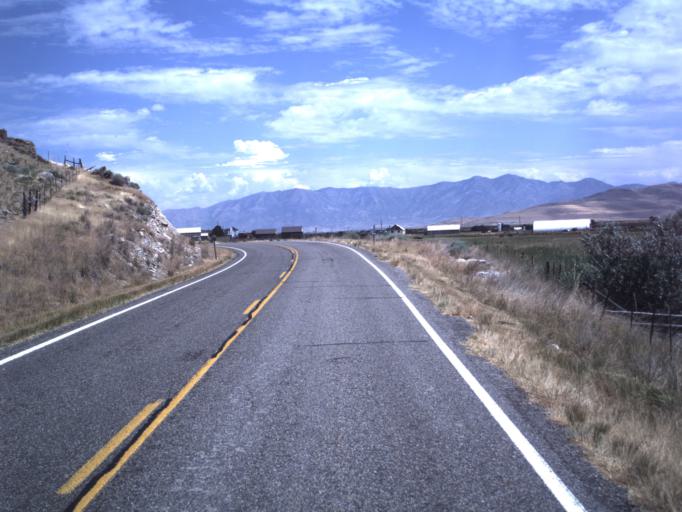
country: US
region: Utah
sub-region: Box Elder County
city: Tremonton
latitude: 41.6224
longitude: -112.3505
